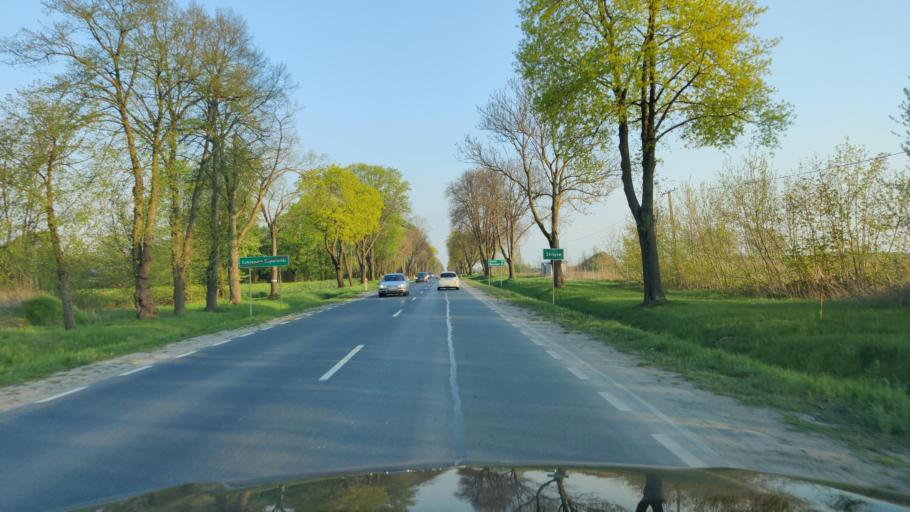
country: PL
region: Masovian Voivodeship
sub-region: Powiat pultuski
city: Pultusk
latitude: 52.6307
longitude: 21.0974
